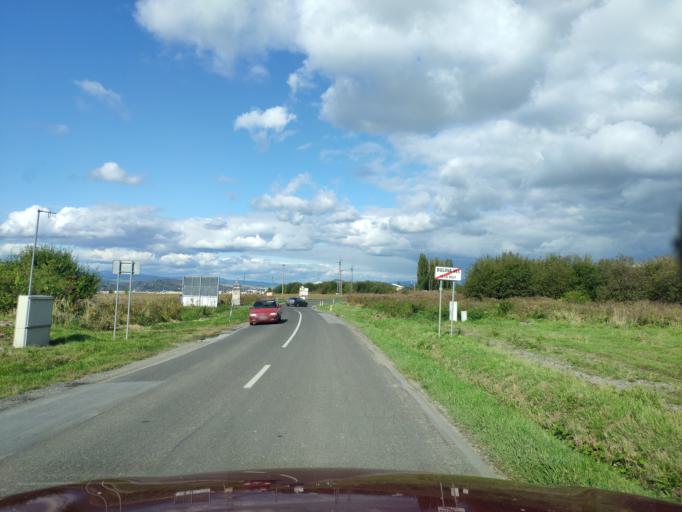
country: SK
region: Presovsky
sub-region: Okres Presov
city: Presov
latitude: 48.9649
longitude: 21.2823
